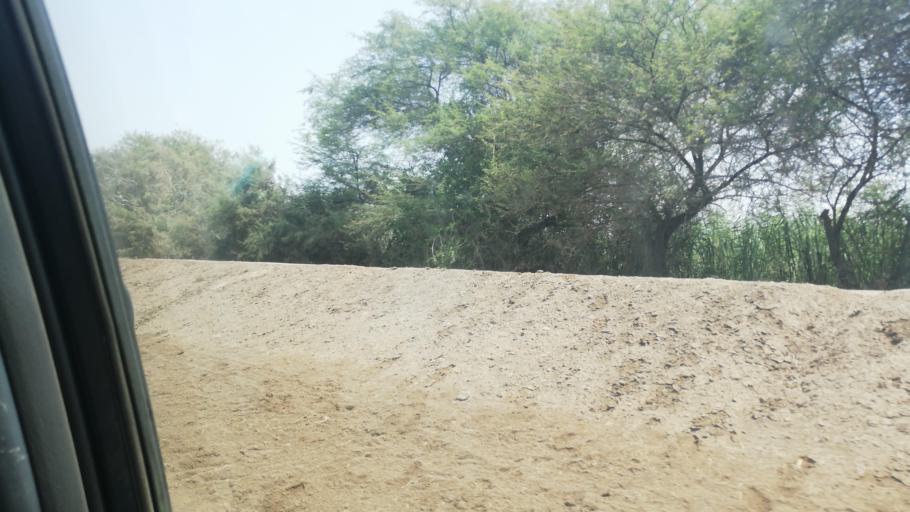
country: SN
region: Saint-Louis
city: Saint-Louis
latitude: 16.4070
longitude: -16.2982
